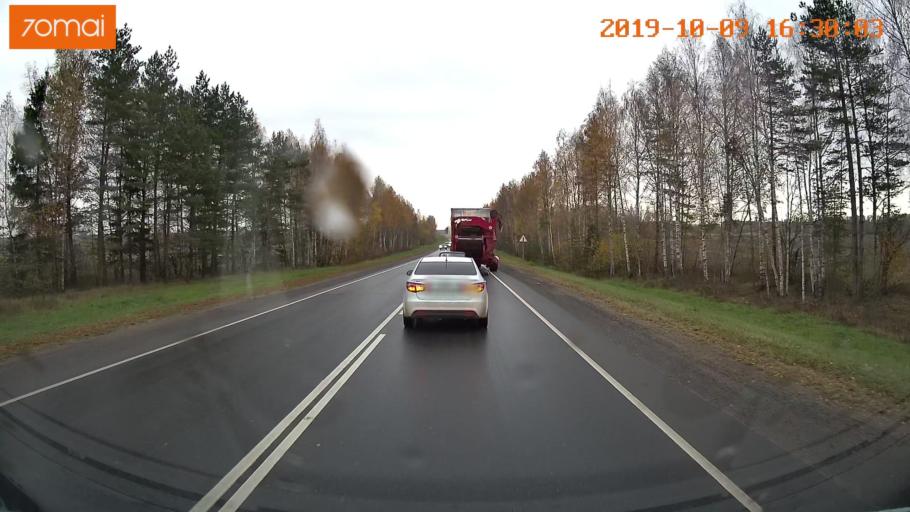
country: RU
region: Kostroma
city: Oktyabr'skiy
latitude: 57.6214
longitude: 40.9383
